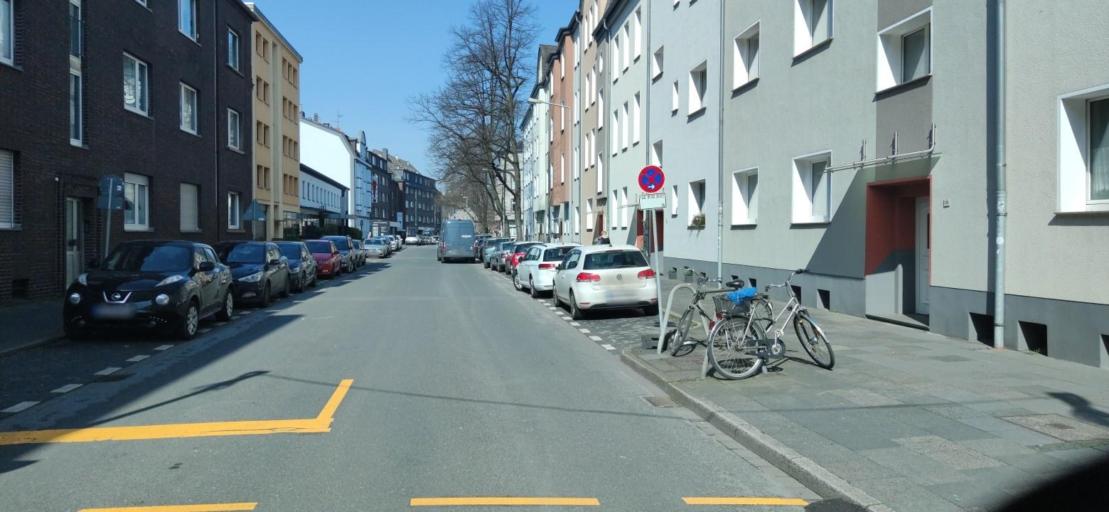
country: DE
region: North Rhine-Westphalia
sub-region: Regierungsbezirk Dusseldorf
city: Duisburg
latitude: 51.4379
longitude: 6.7775
